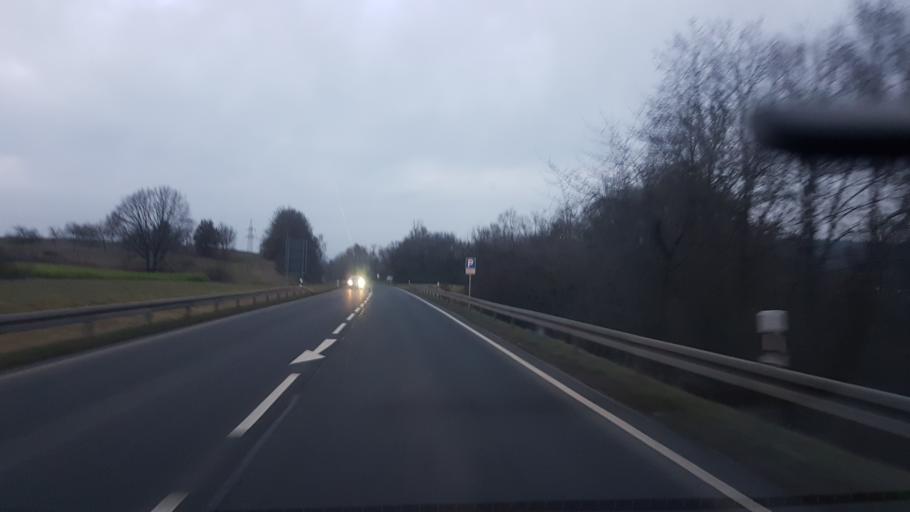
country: DE
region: Bavaria
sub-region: Regierungsbezirk Unterfranken
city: Rentweinsdorf
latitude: 50.0957
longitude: 10.7863
